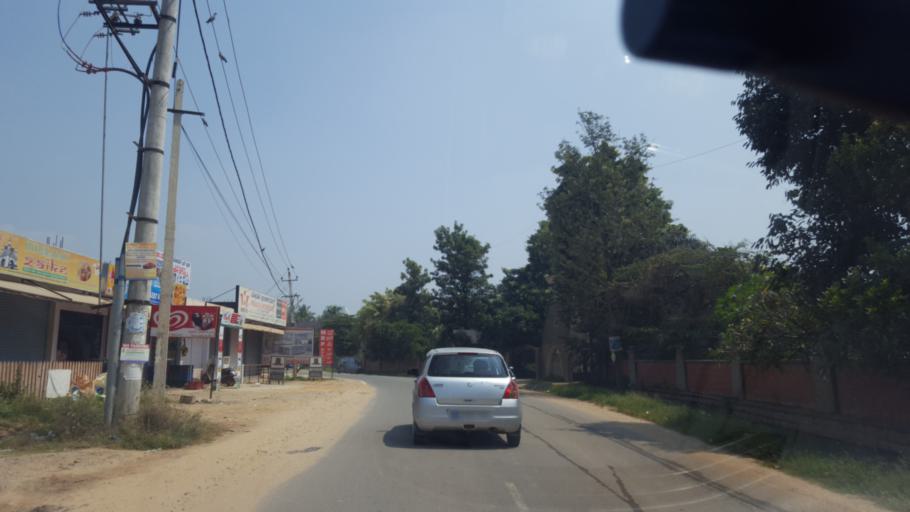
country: IN
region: Karnataka
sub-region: Bangalore Urban
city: Bangalore
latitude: 12.9381
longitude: 77.7146
